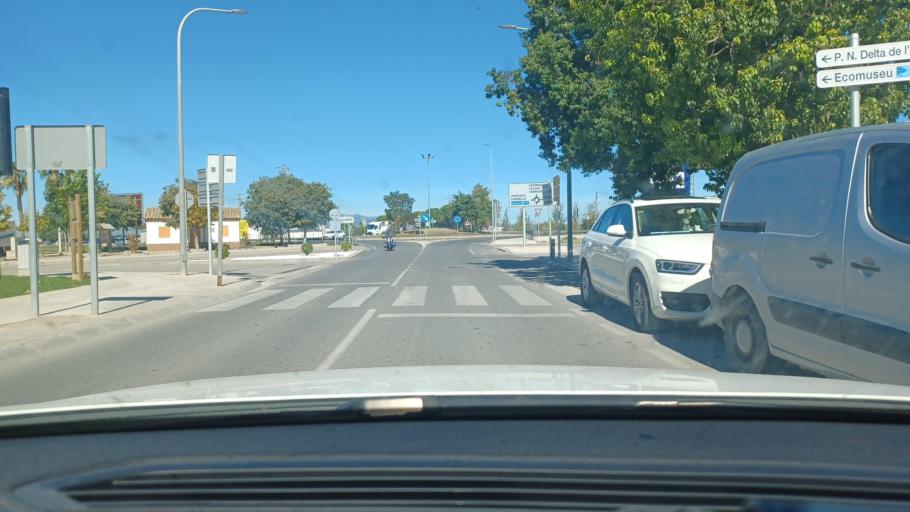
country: ES
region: Catalonia
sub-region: Provincia de Tarragona
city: Deltebre
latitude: 40.7231
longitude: 0.7250
